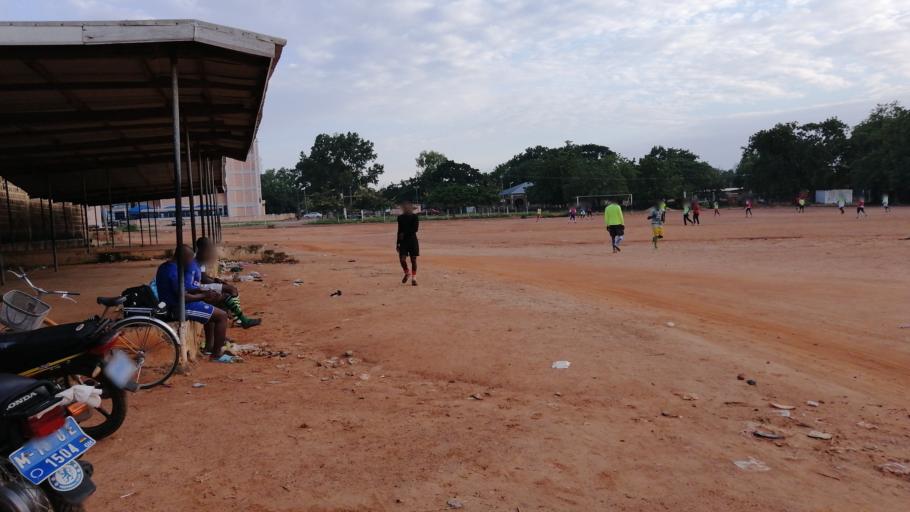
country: GH
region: Upper East
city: Bolgatanga
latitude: 10.7908
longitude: -0.8549
